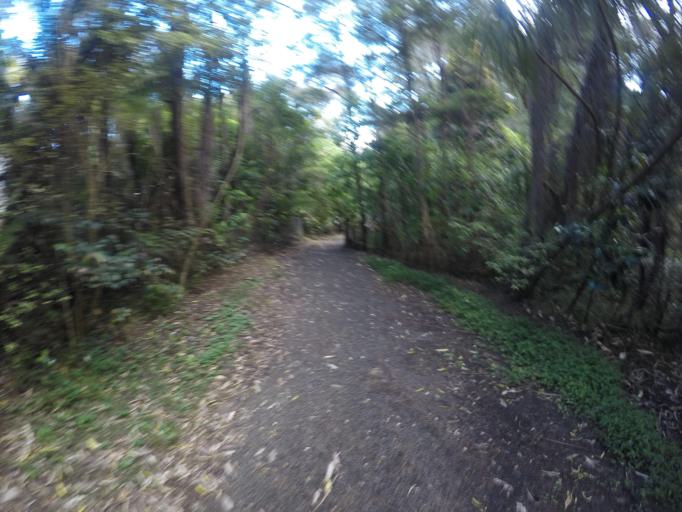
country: NZ
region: Auckland
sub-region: Auckland
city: Titirangi
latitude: -36.9299
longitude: 174.6514
